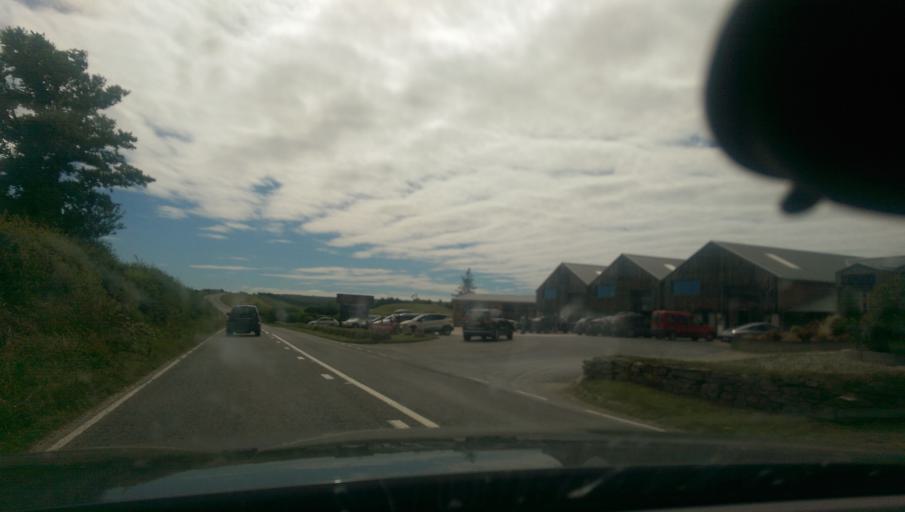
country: GB
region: England
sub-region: Cornwall
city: Wadebridge
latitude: 50.5056
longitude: -4.8844
